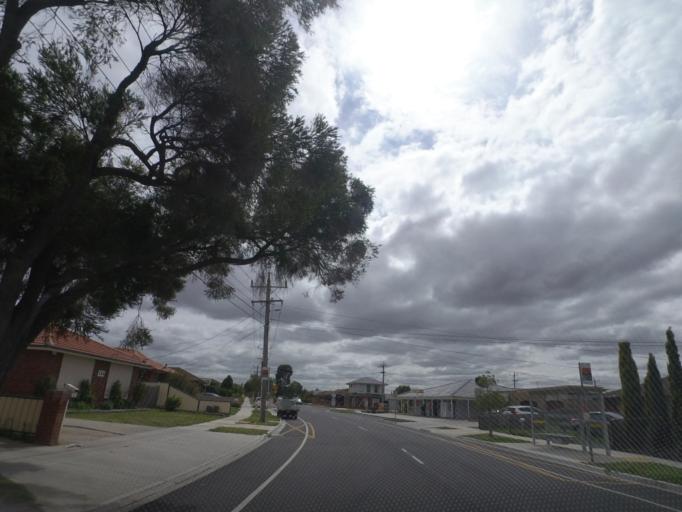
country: AU
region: Victoria
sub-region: Brimbank
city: Deer Park
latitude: -37.7534
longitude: 144.7617
